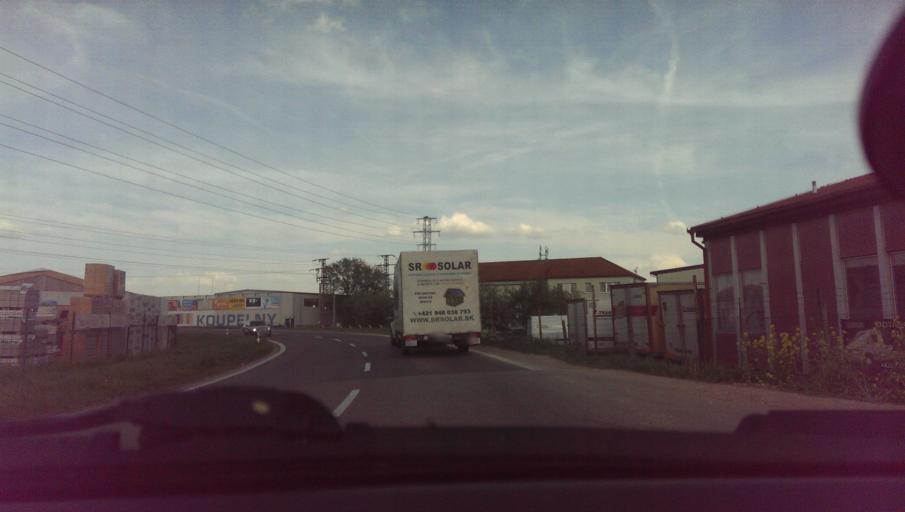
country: CZ
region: Zlin
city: Uhersky Brod
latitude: 49.0180
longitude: 17.6352
